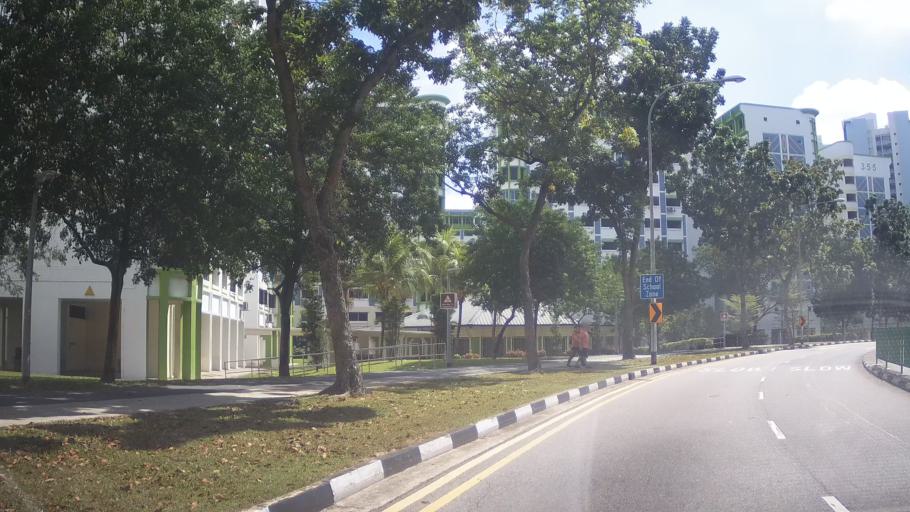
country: MY
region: Johor
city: Johor Bahru
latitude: 1.3381
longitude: 103.7197
